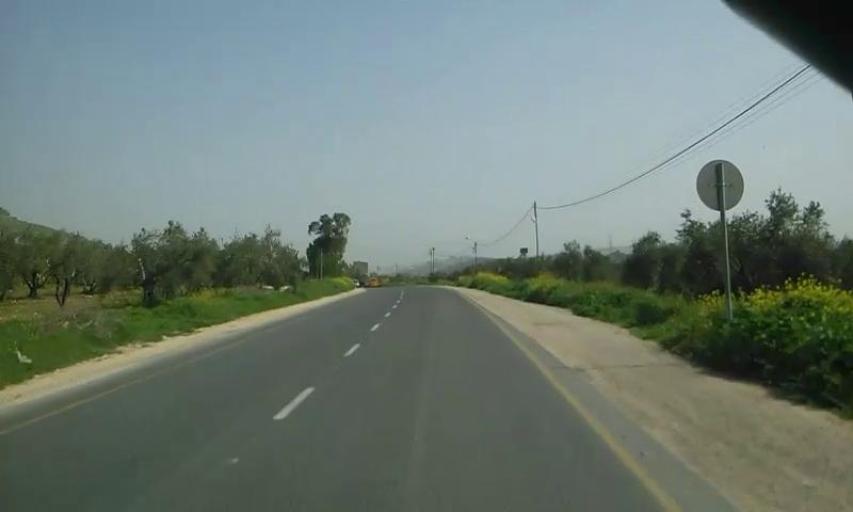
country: PS
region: West Bank
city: Huwwarah
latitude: 32.1669
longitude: 35.2653
